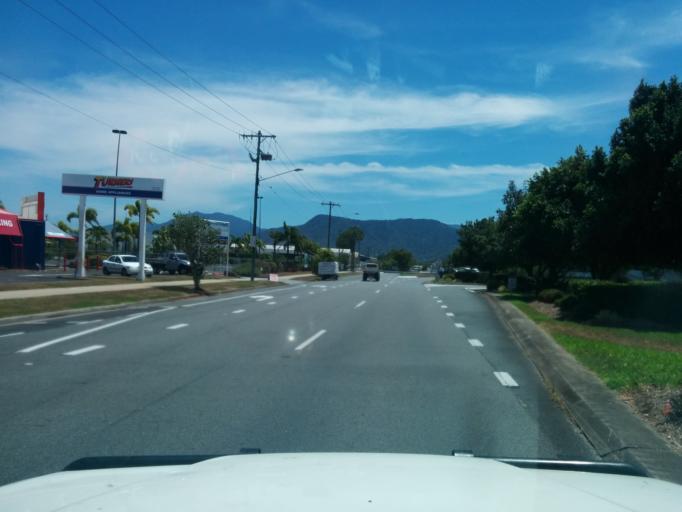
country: AU
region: Queensland
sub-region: Cairns
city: Cairns
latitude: -16.9309
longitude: 145.7683
